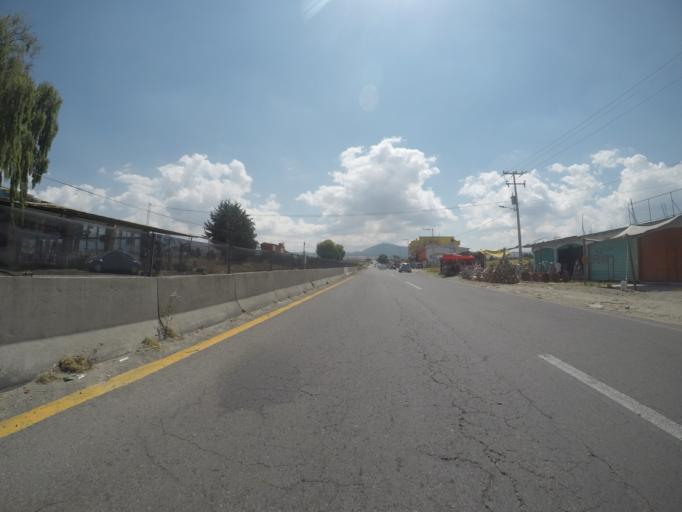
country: MX
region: Mexico
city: San Juan de las Huertas
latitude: 19.2424
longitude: -99.7697
